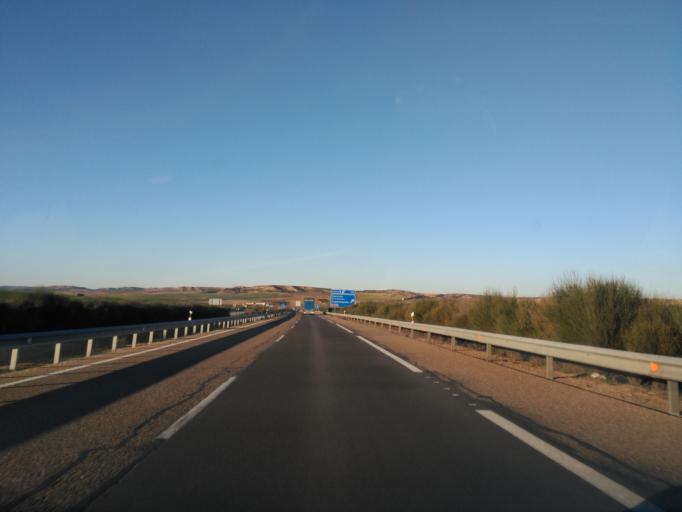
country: ES
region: Castille and Leon
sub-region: Provincia de Zamora
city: Castrillo de la Guarena
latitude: 41.2152
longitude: -5.3208
